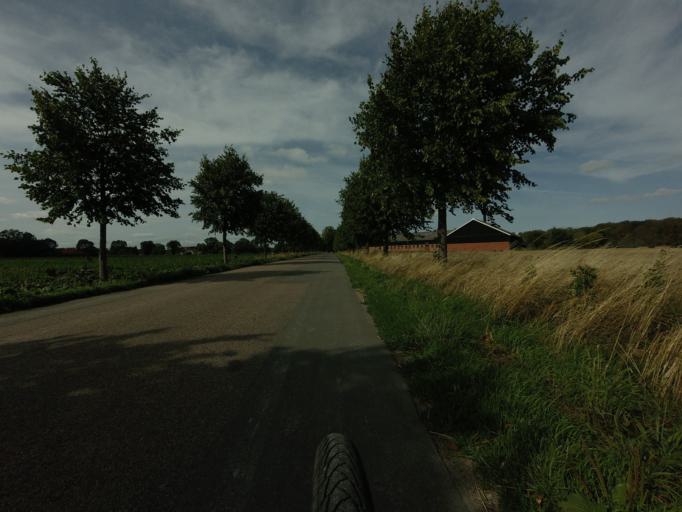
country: DK
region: Zealand
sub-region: Faxe Kommune
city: Fakse Ladeplads
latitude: 55.2507
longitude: 12.2269
